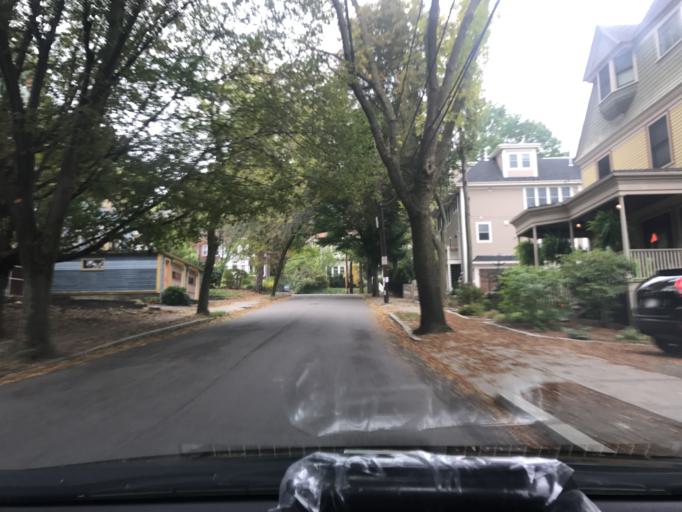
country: US
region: Massachusetts
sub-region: Norfolk County
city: Brookline
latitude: 42.3451
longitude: -71.1295
